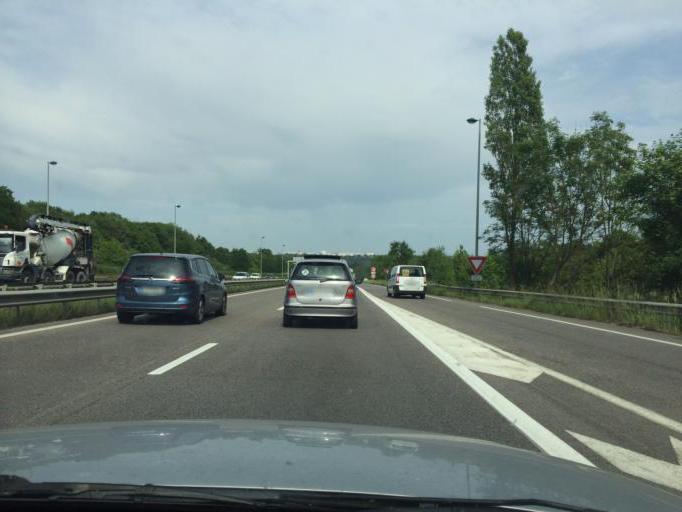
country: FR
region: Lorraine
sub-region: Departement de Meurthe-et-Moselle
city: Velaine-en-Haye
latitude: 48.6931
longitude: 6.0748
